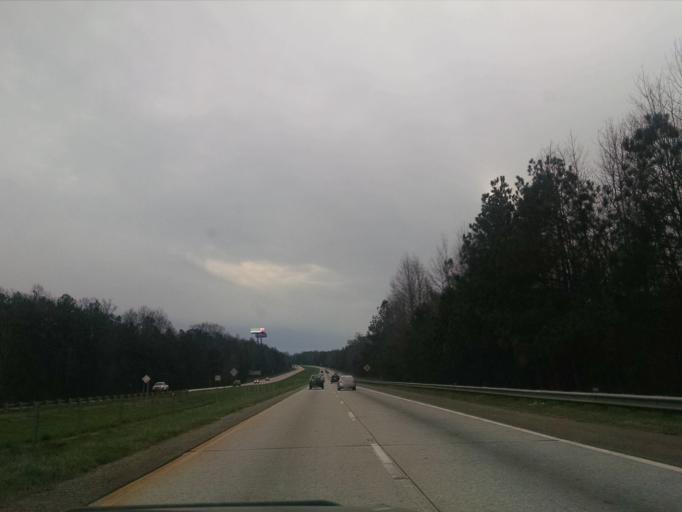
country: US
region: Georgia
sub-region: Hall County
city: Flowery Branch
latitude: 34.1788
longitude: -83.9146
